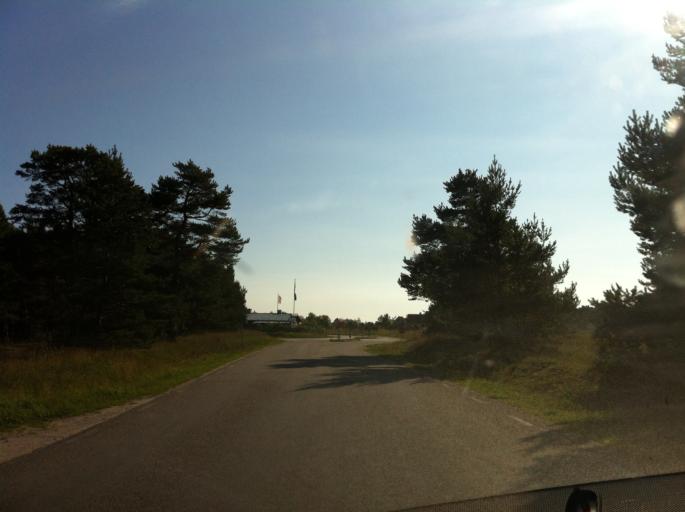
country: SE
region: Gotland
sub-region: Gotland
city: Slite
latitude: 57.9585
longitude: 19.2374
